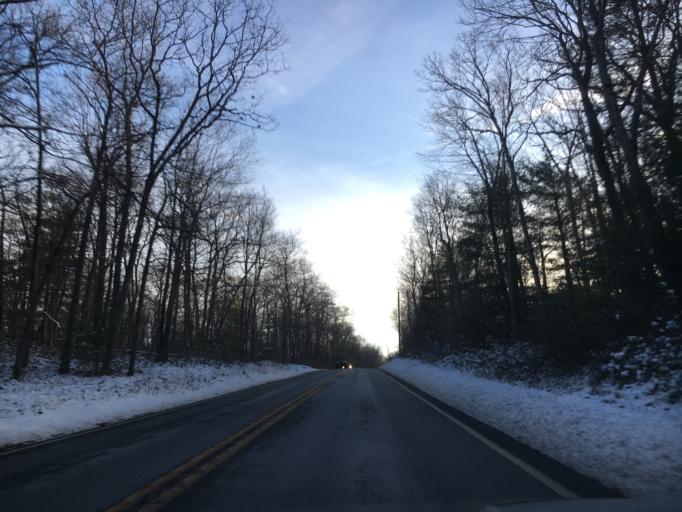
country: US
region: Pennsylvania
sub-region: Pike County
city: Hemlock Farms
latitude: 41.3608
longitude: -75.1282
